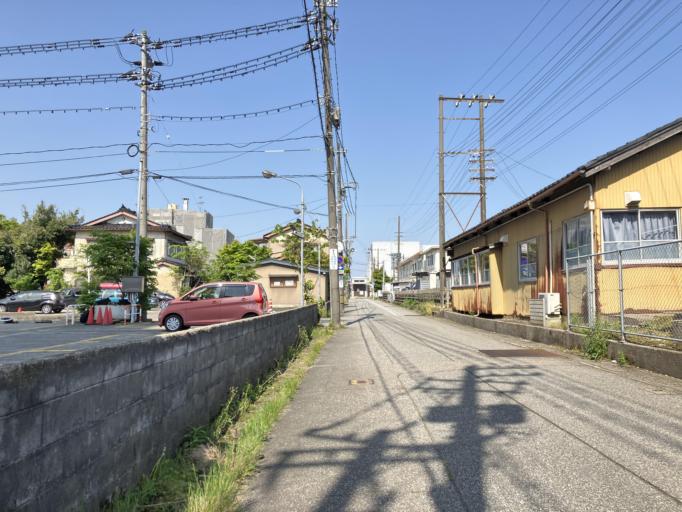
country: JP
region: Toyama
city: Takaoka
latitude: 36.7404
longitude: 137.0173
